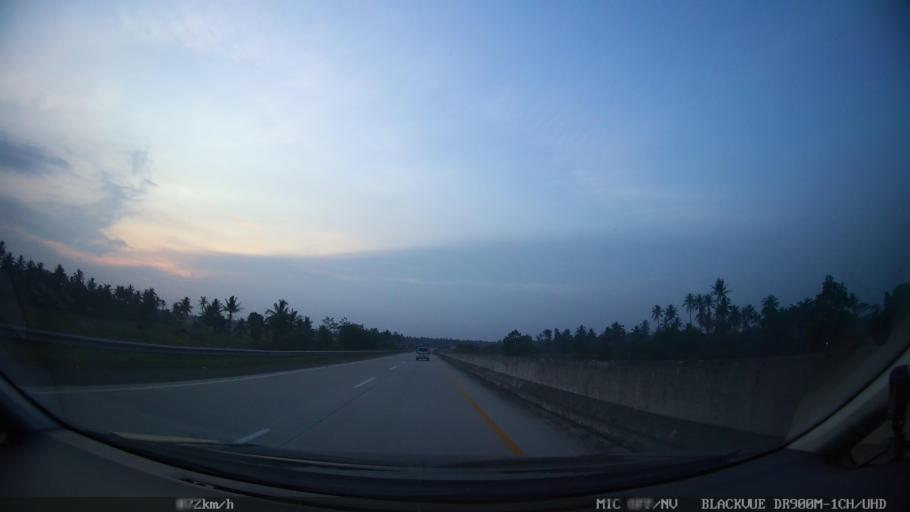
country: ID
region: Lampung
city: Kalianda
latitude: -5.6674
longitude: 105.5984
